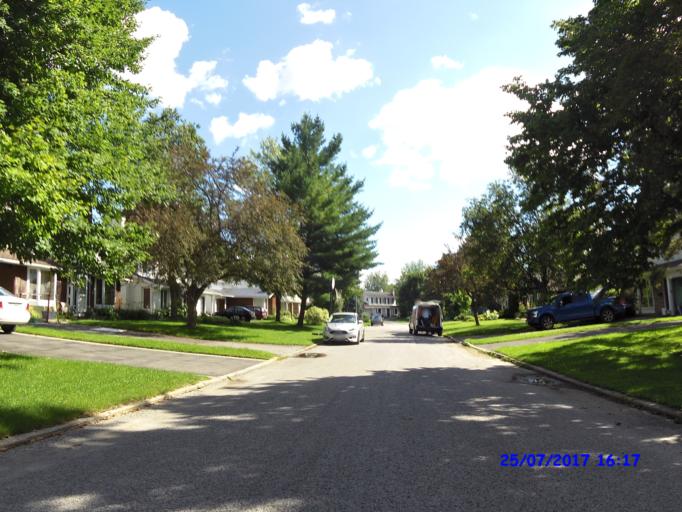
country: CA
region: Ontario
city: Ottawa
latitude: 45.3557
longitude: -75.7201
